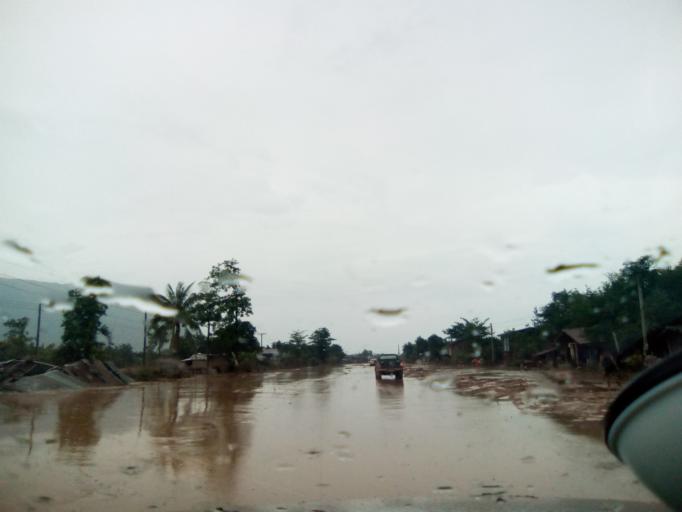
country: LA
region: Attapu
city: Attapu
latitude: 14.7033
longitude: 106.5242
